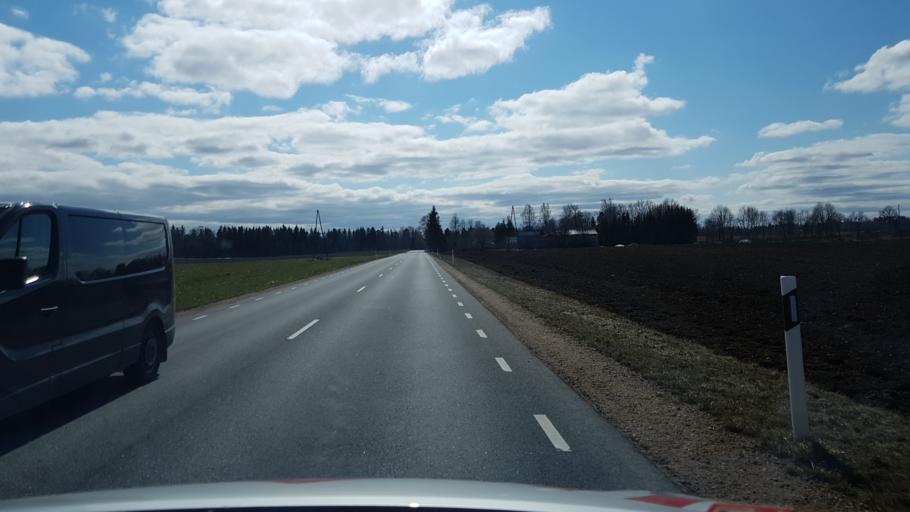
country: EE
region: Laeaene-Virumaa
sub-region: Tapa vald
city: Tapa
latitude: 59.3662
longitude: 26.0012
